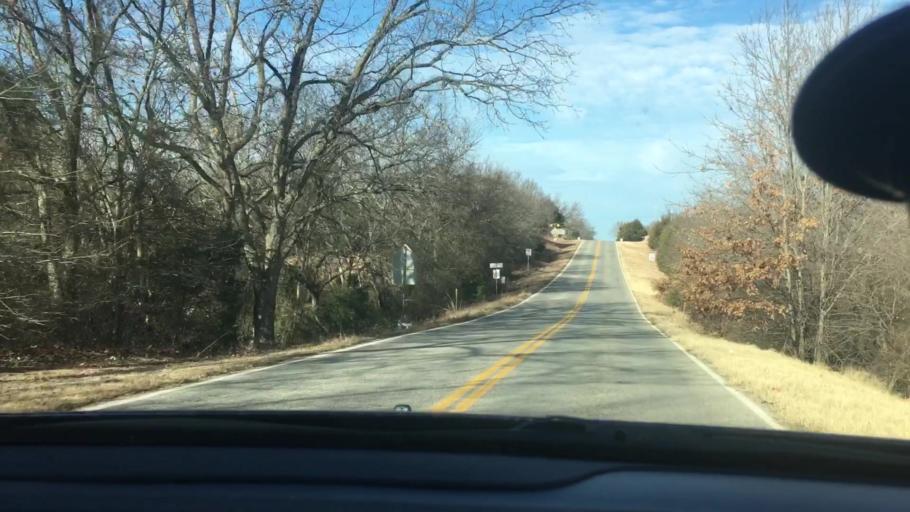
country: US
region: Oklahoma
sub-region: Seminole County
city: Konawa
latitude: 34.9610
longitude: -96.7616
